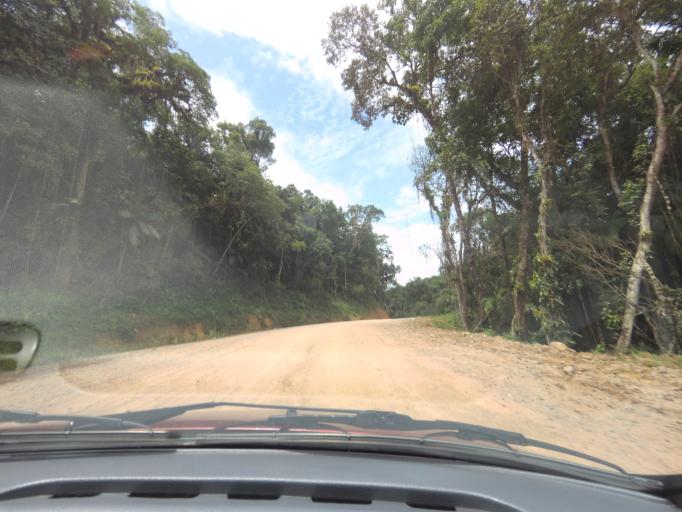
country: BR
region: Santa Catarina
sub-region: Brusque
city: Brusque
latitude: -27.0754
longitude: -48.9756
